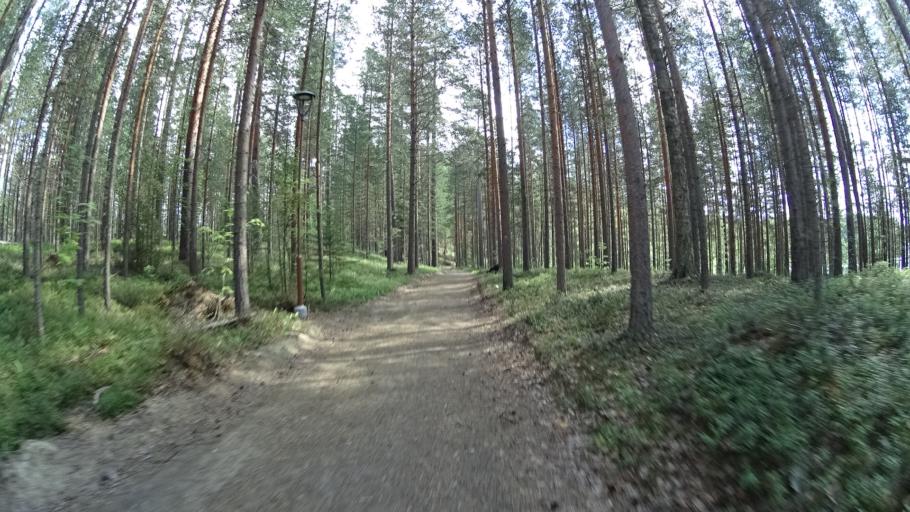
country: FI
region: Southern Savonia
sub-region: Savonlinna
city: Punkaharju
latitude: 61.7914
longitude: 29.3050
